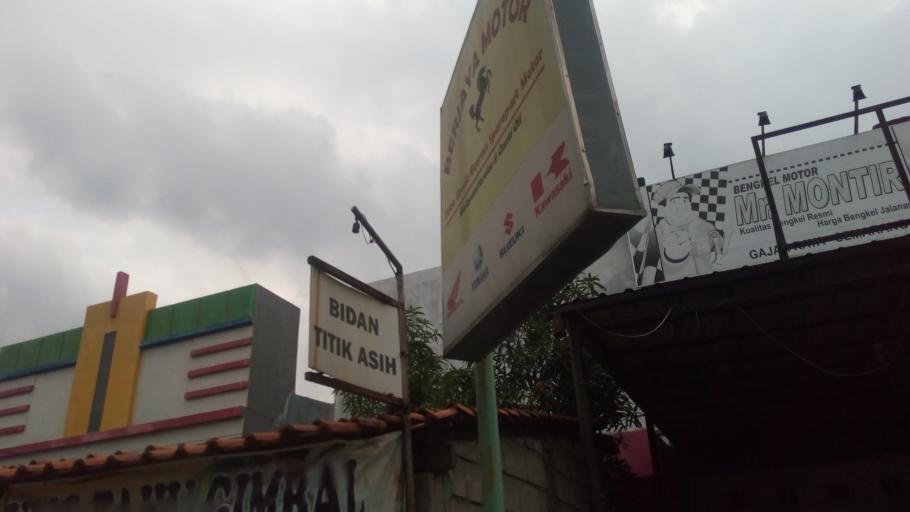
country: ID
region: Central Java
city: Mranggen
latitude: -7.0549
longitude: 110.4715
